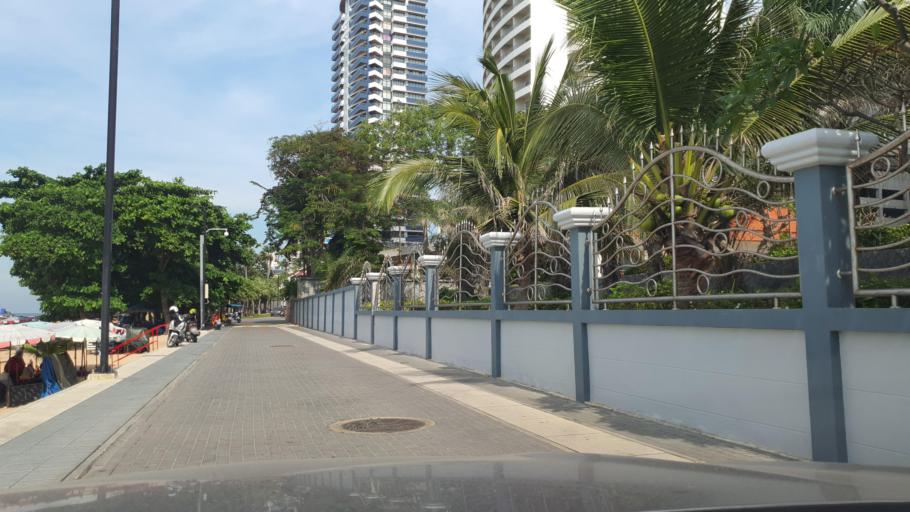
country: TH
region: Chon Buri
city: Phatthaya
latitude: 12.9070
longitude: 100.8593
